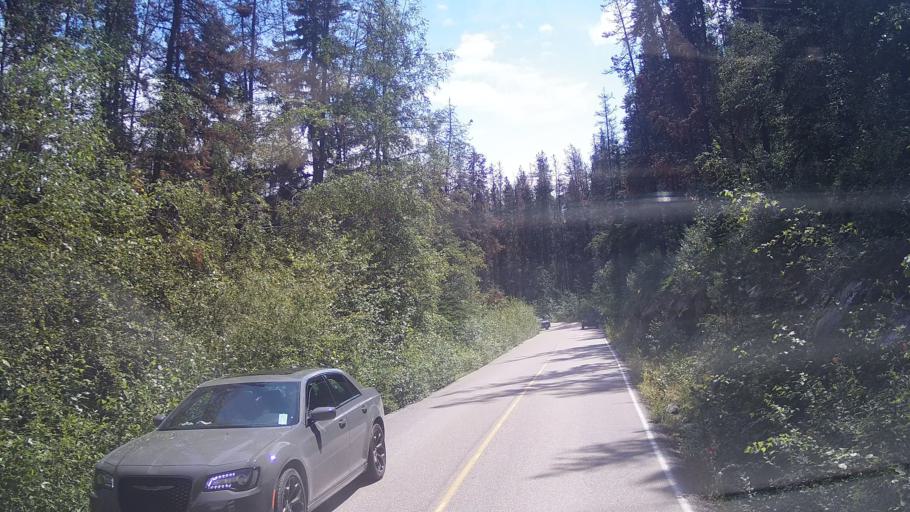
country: CA
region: Alberta
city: Jasper Park Lodge
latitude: 52.7676
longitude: -118.0272
